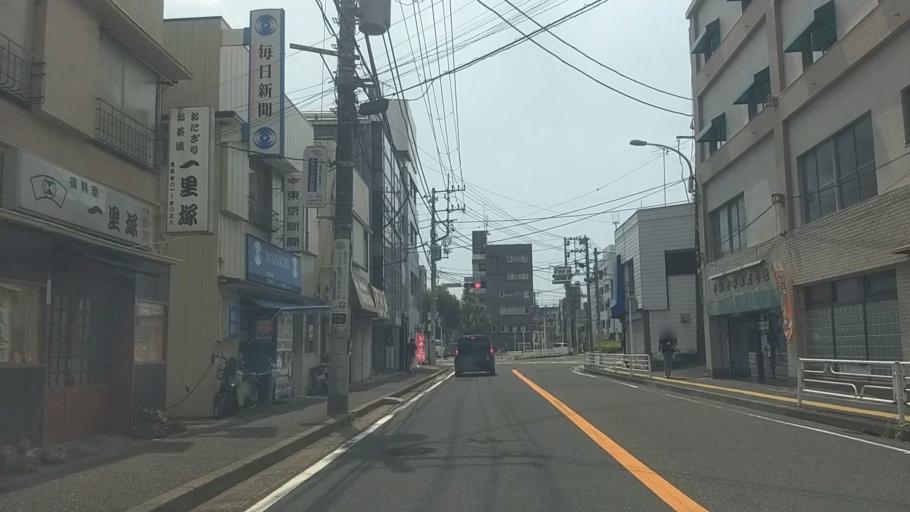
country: JP
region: Kanagawa
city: Yokohama
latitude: 35.4930
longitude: 139.6456
